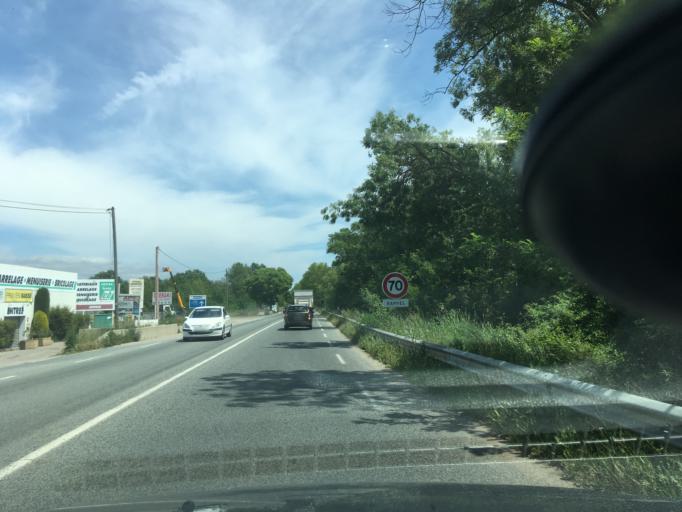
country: FR
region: Provence-Alpes-Cote d'Azur
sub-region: Departement du Var
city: Roquebrune-sur-Argens
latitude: 43.4623
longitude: 6.6487
